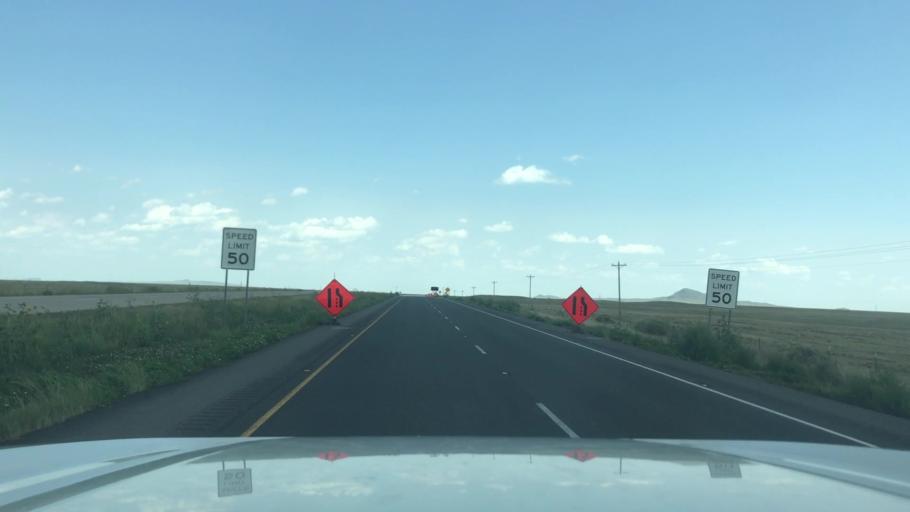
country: US
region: New Mexico
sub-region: Union County
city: Clayton
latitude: 36.6185
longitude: -103.6919
